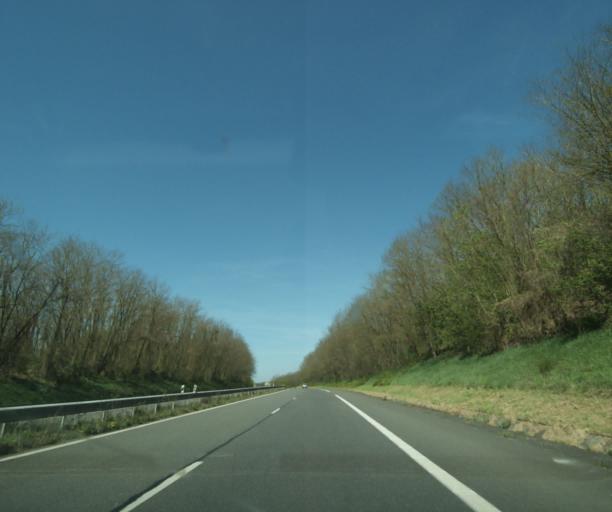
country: FR
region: Bourgogne
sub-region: Departement de la Nievre
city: Chaulgnes
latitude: 47.1106
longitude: 3.0685
